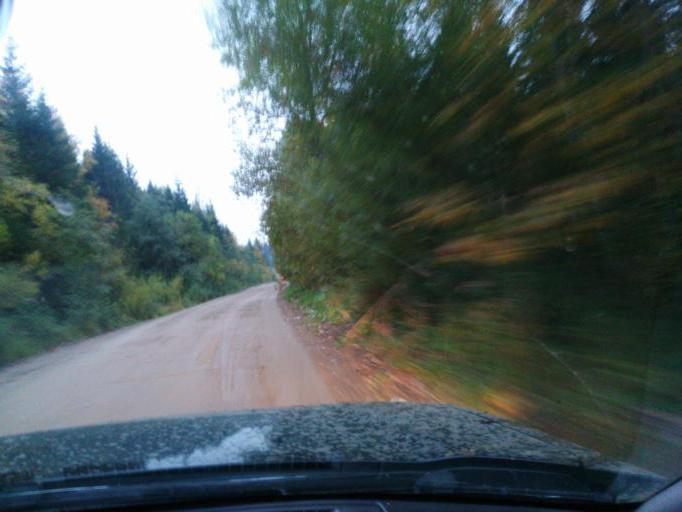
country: RU
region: Sverdlovsk
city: Sylva
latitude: 57.7998
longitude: 58.5478
